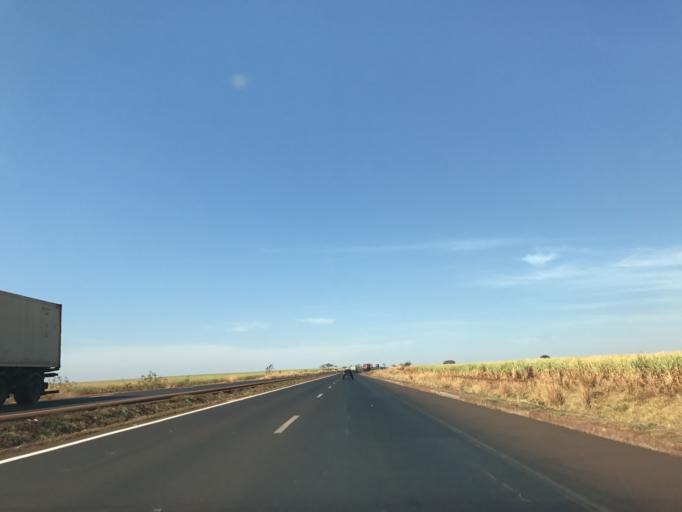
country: BR
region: Minas Gerais
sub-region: Centralina
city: Centralina
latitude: -18.5104
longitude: -49.1892
